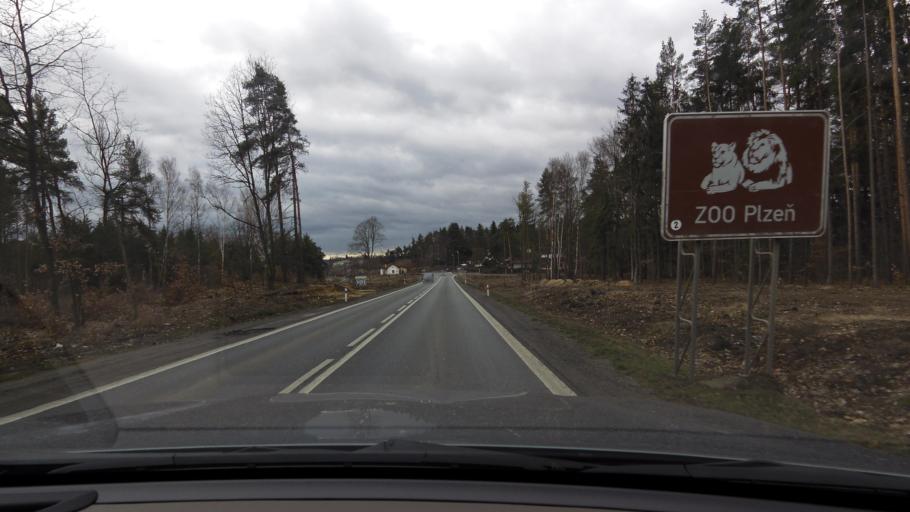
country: CZ
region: Plzensky
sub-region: Okres Plzen-Sever
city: Tremosna
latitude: 49.7909
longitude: 13.3845
